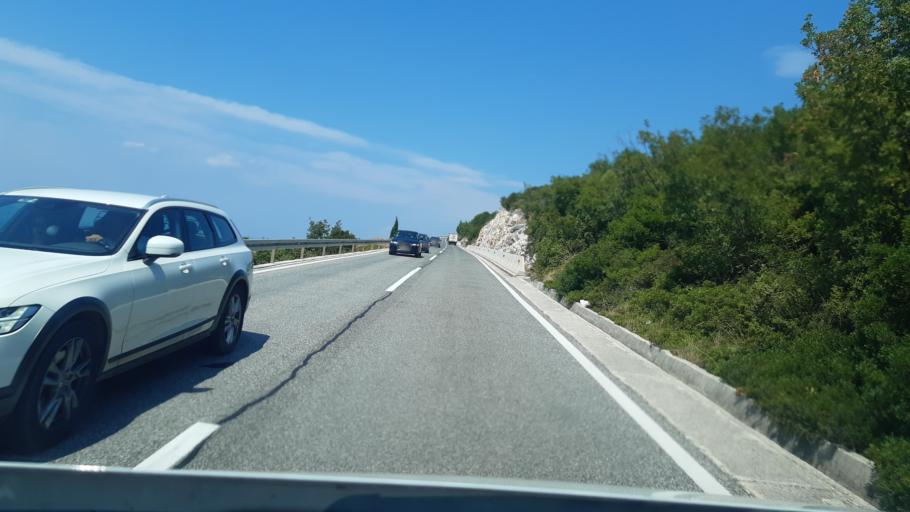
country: HR
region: Dubrovacko-Neretvanska
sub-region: Grad Dubrovnik
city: Opuzen
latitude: 42.9614
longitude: 17.5216
